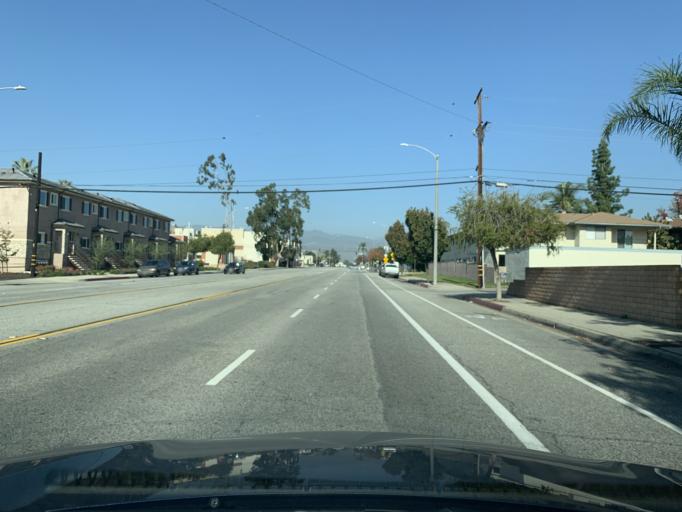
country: US
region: California
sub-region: Los Angeles County
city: Covina
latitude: 34.0842
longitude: -117.8878
